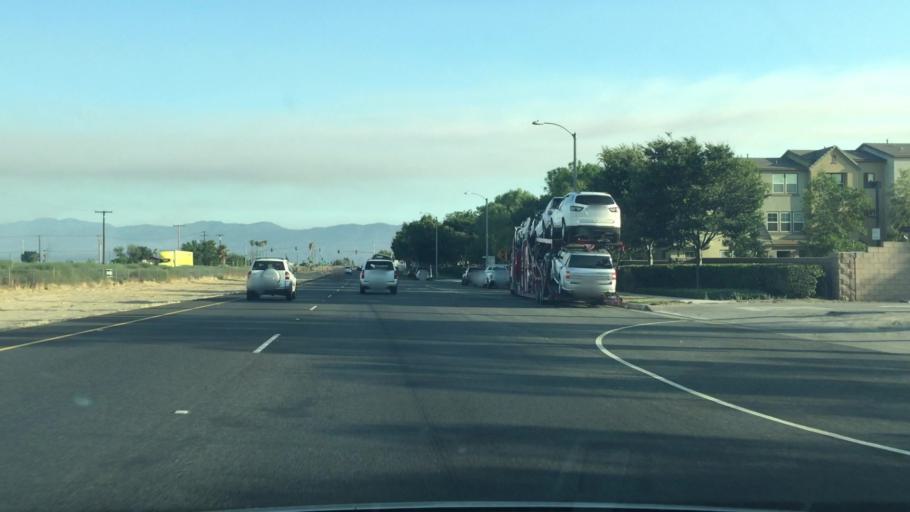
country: US
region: California
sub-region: San Bernardino County
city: Chino
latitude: 34.0150
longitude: -117.6509
